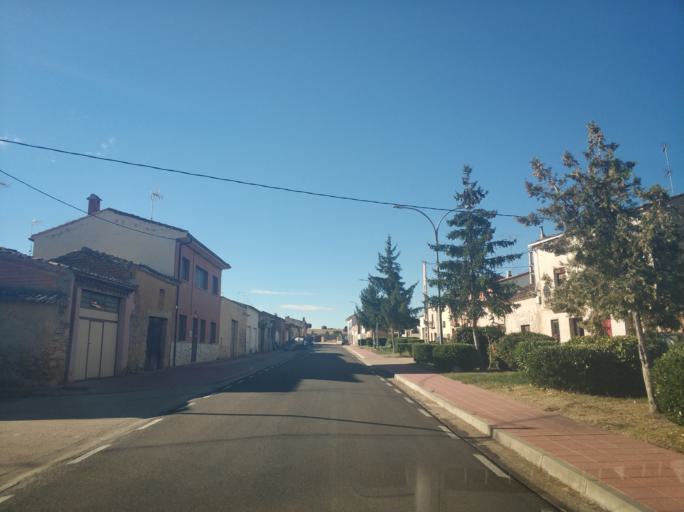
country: ES
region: Castille and Leon
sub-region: Provincia de Burgos
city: San Juan del Monte
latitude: 41.6826
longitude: -3.5235
